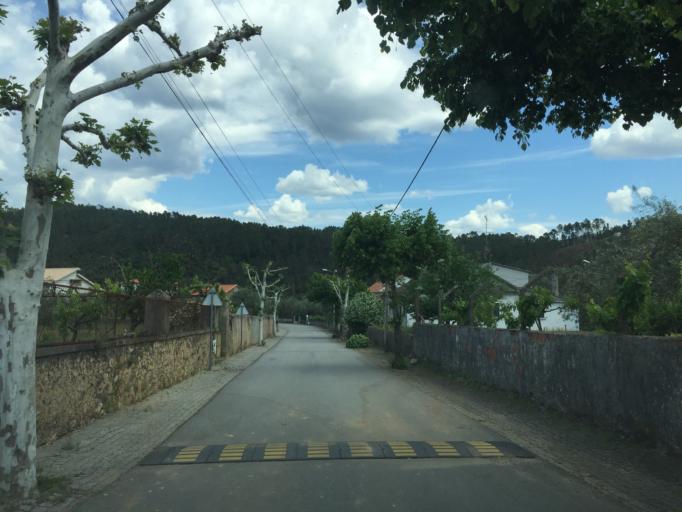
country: PT
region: Coimbra
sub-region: Pampilhosa da Serra
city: Pampilhosa da Serra
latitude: 40.0455
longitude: -7.8074
